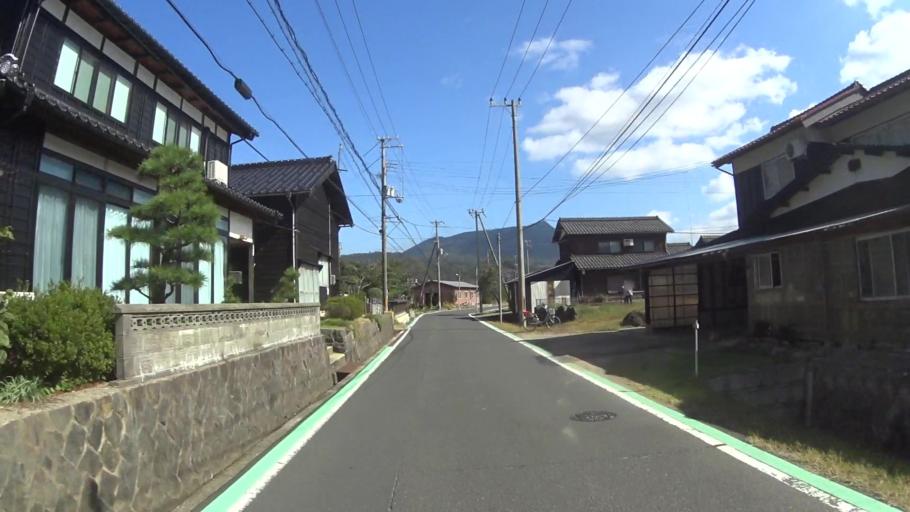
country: JP
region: Kyoto
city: Miyazu
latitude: 35.7113
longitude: 135.1020
